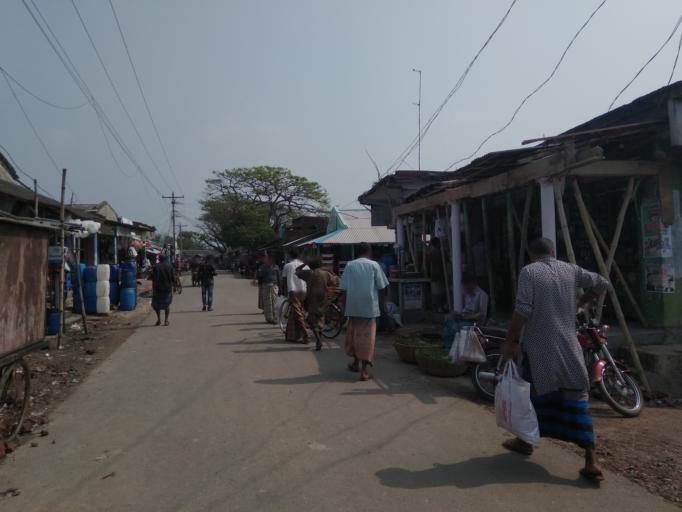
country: IN
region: West Bengal
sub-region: North 24 Parganas
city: Gosaba
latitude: 22.2286
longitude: 89.1554
